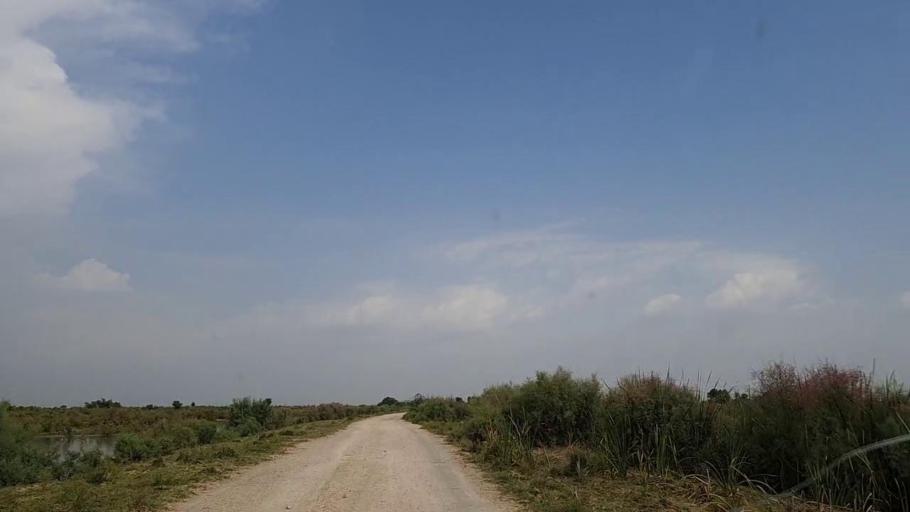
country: PK
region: Sindh
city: Khanpur
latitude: 27.8279
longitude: 69.5131
